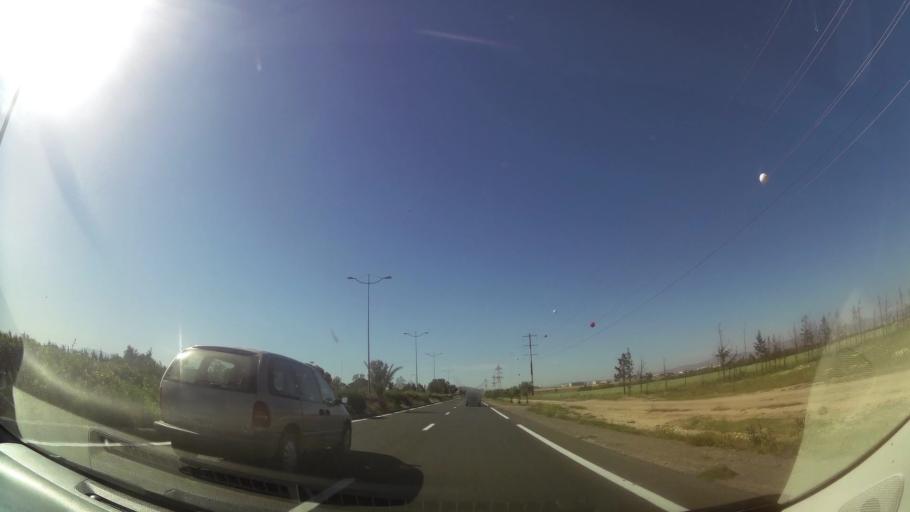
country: MA
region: Oriental
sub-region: Oujda-Angad
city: Oujda
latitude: 34.7532
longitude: -1.9345
